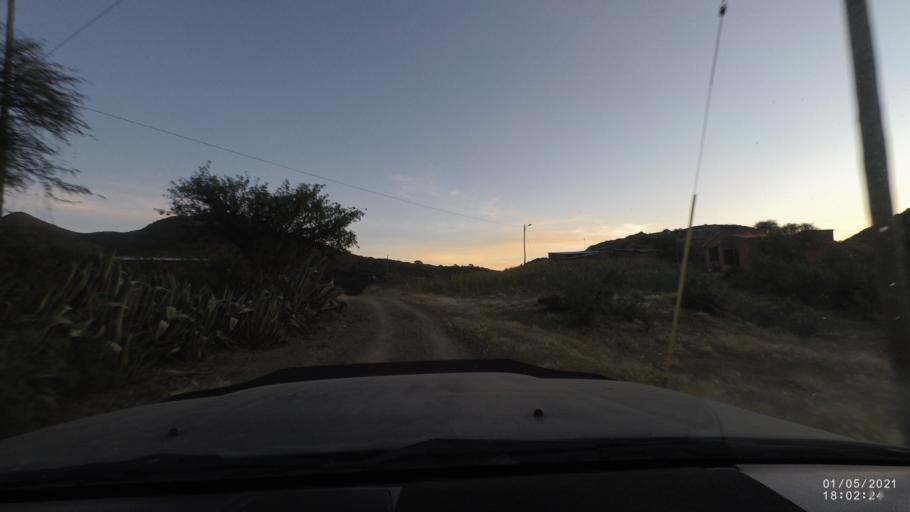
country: BO
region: Cochabamba
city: Capinota
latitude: -17.6876
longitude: -66.1738
